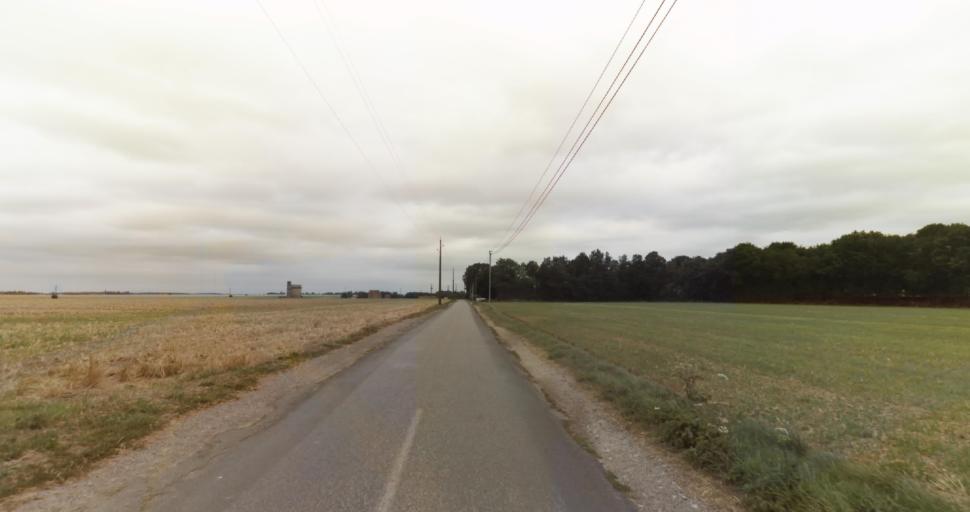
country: FR
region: Haute-Normandie
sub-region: Departement de l'Eure
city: La Couture-Boussey
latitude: 48.9309
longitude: 1.3331
